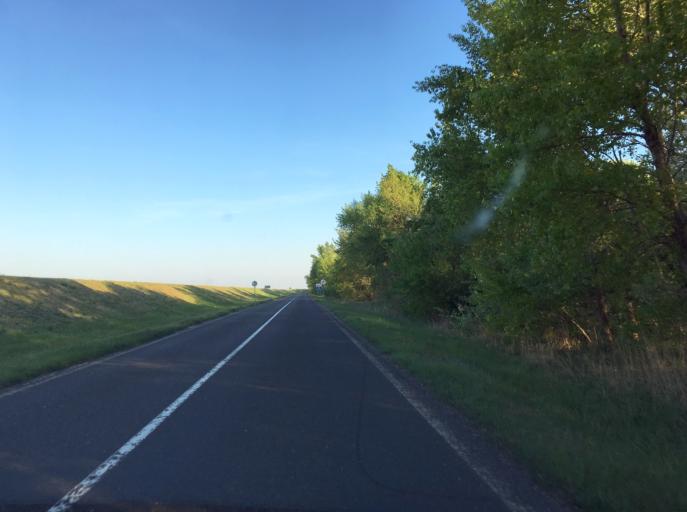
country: HU
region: Gyor-Moson-Sopron
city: Rajka
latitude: 48.0312
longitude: 17.2366
